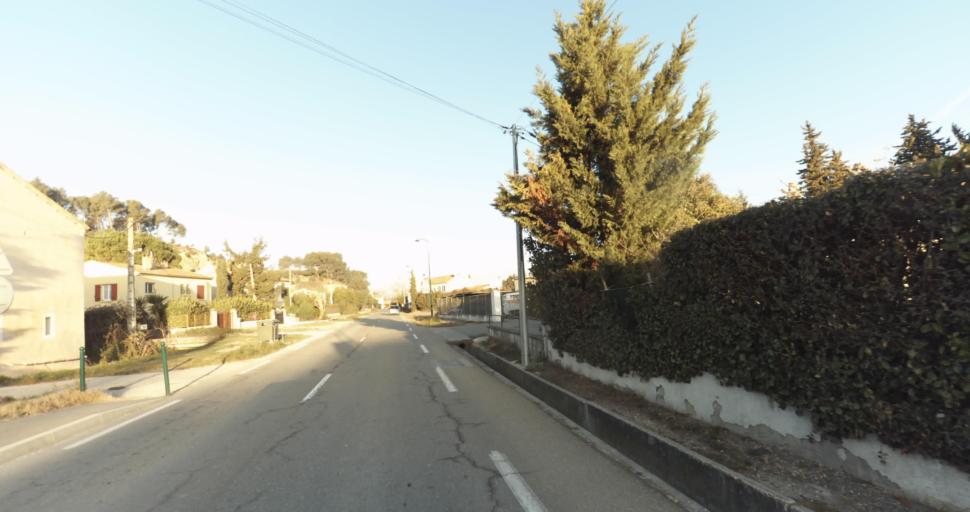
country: FR
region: Provence-Alpes-Cote d'Azur
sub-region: Departement des Bouches-du-Rhone
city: Barbentane
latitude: 43.9005
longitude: 4.7626
